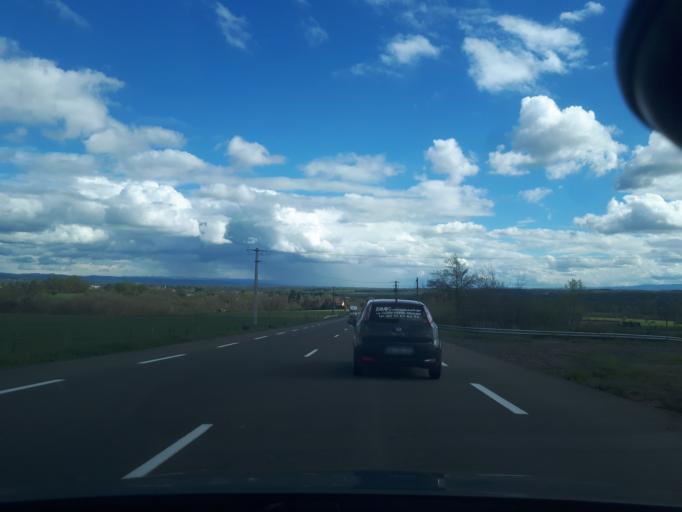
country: FR
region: Rhone-Alpes
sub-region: Departement de la Loire
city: Balbigny
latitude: 45.8366
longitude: 4.1682
